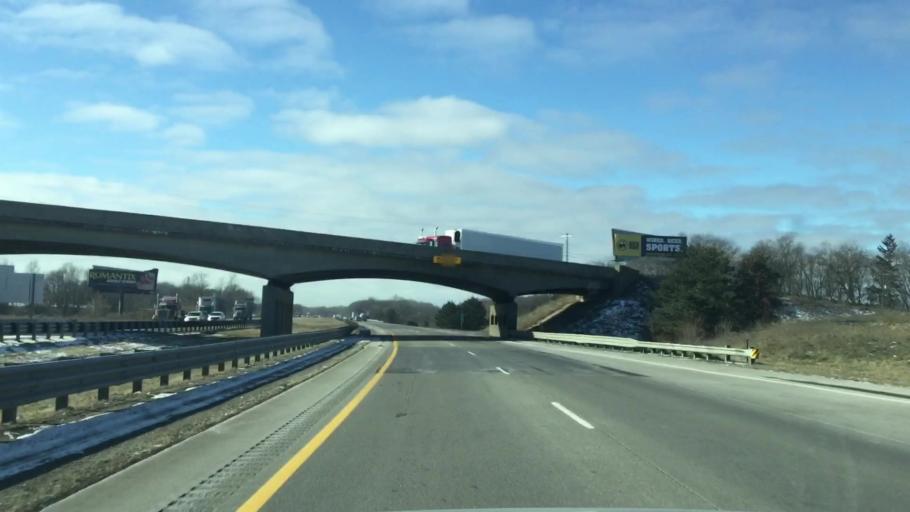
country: US
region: Michigan
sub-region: Calhoun County
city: Brownlee Park
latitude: 42.3000
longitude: -85.0851
